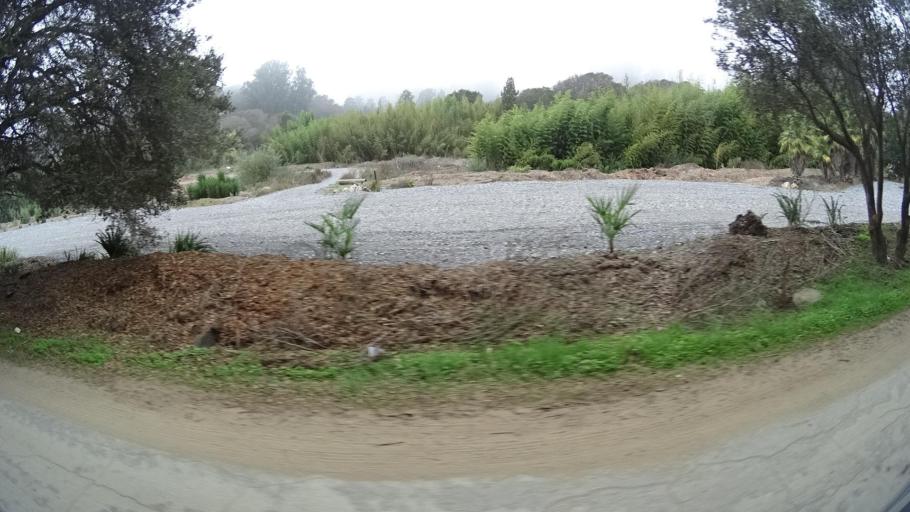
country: US
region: California
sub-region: Monterey County
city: Las Lomas
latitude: 36.8738
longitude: -121.7196
